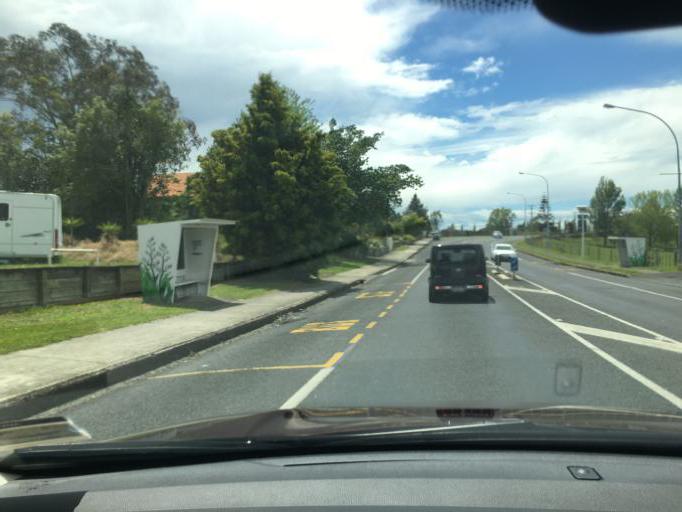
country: NZ
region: Waikato
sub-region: Hamilton City
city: Hamilton
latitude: -37.9179
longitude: 175.3067
